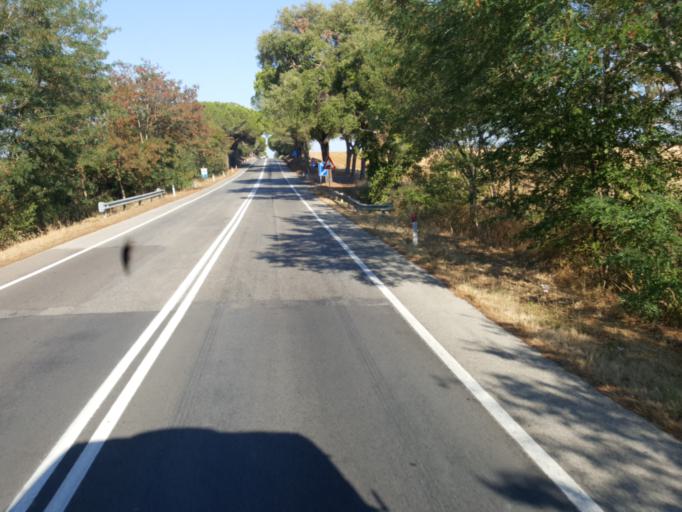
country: IT
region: Latium
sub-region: Provincia di Viterbo
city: Pescia Romana
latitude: 42.4143
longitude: 11.4504
